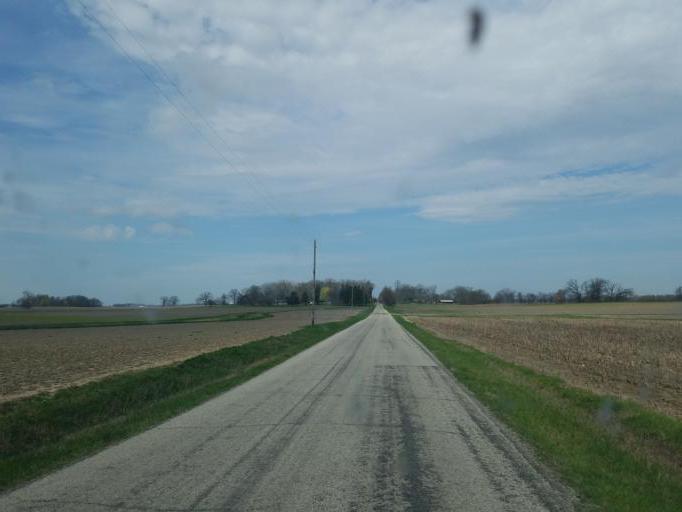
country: US
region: Ohio
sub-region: Crawford County
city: Bucyrus
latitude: 40.7467
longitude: -83.0146
